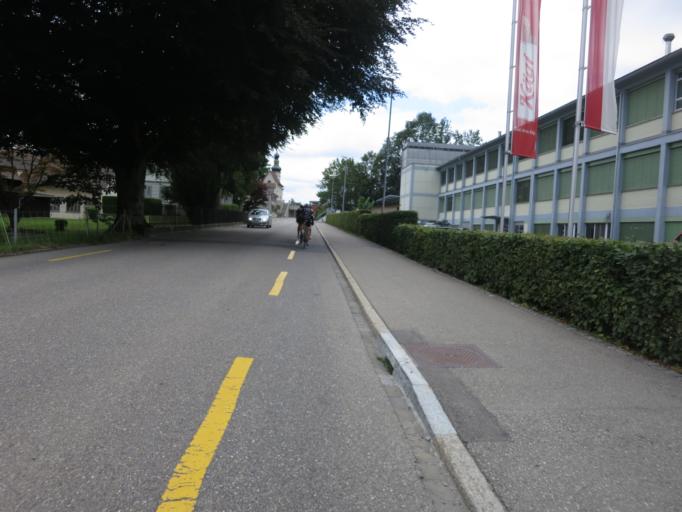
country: CH
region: Saint Gallen
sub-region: Wahlkreis Toggenburg
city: Lichtensteig
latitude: 47.3300
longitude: 9.0848
